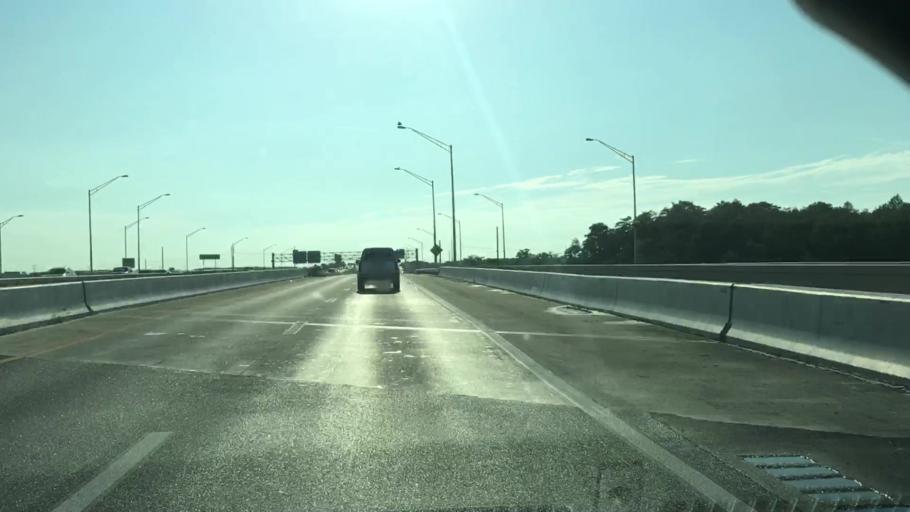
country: US
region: Florida
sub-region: Orange County
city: Meadow Woods
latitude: 28.3680
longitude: -81.3822
